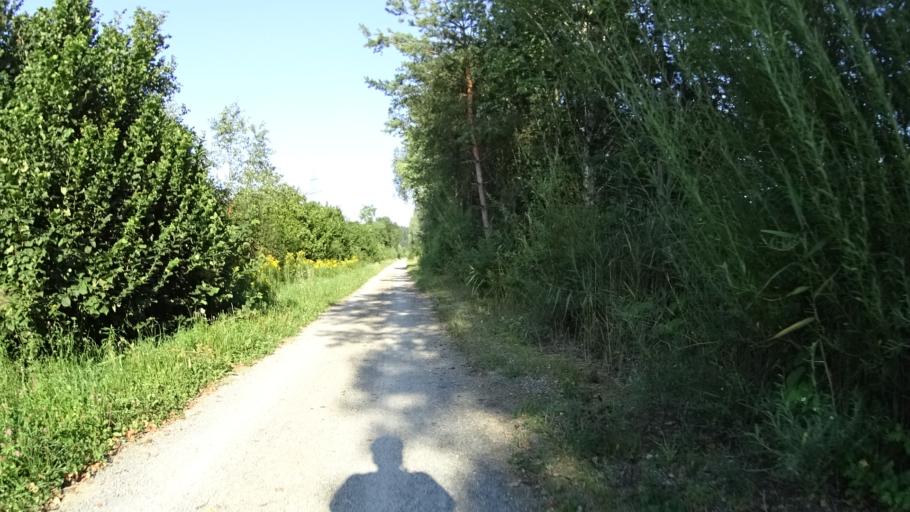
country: AT
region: Carinthia
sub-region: Politischer Bezirk Villach Land
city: Wernberg
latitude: 46.5944
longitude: 13.9718
